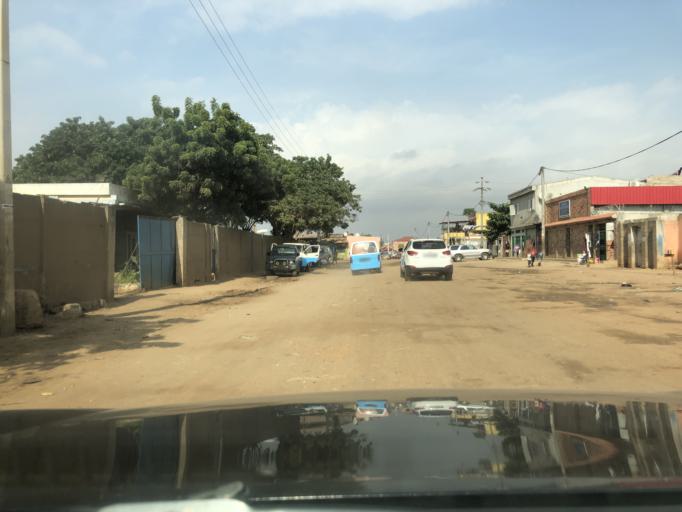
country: AO
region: Luanda
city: Luanda
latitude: -8.8563
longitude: 13.2543
